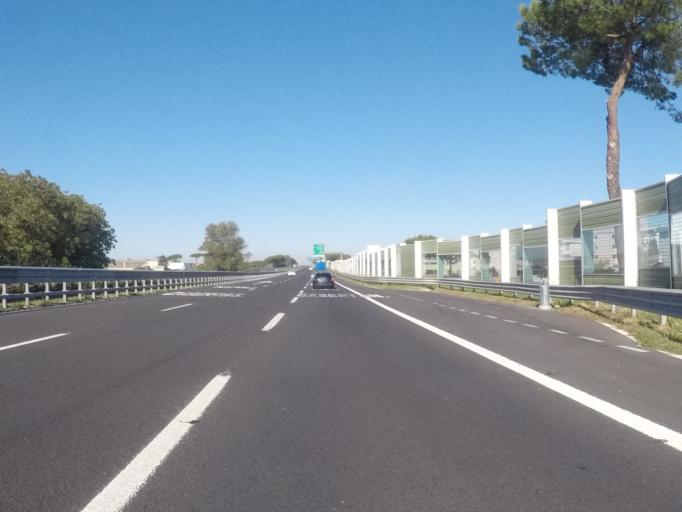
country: IT
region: Campania
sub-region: Provincia di Caserta
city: San Marco Evangelista
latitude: 41.0345
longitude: 14.3320
